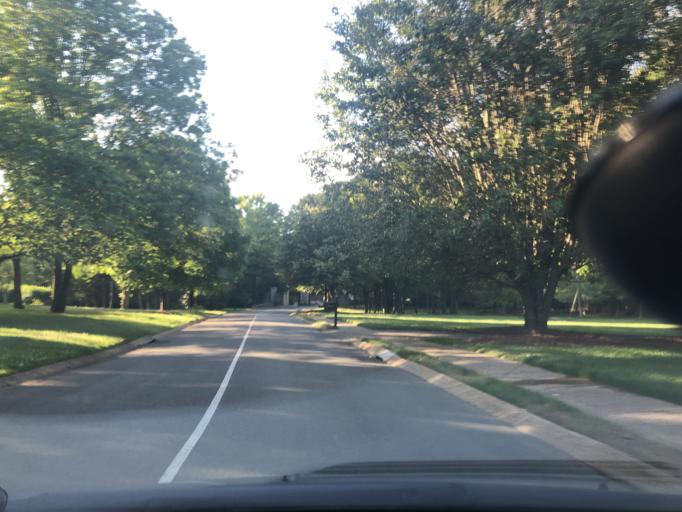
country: US
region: Tennessee
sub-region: Davidson County
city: Forest Hills
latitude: 36.0582
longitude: -86.8346
